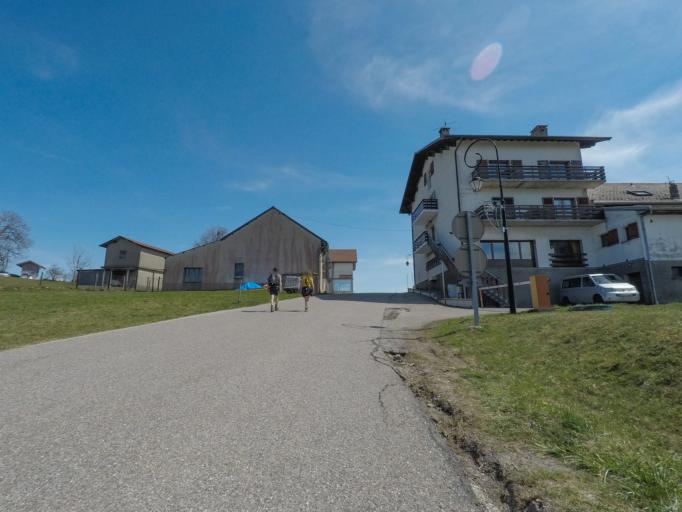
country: FR
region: Rhone-Alpes
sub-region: Departement de la Haute-Savoie
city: Collonges-sous-Saleve
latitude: 46.1200
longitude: 6.1709
